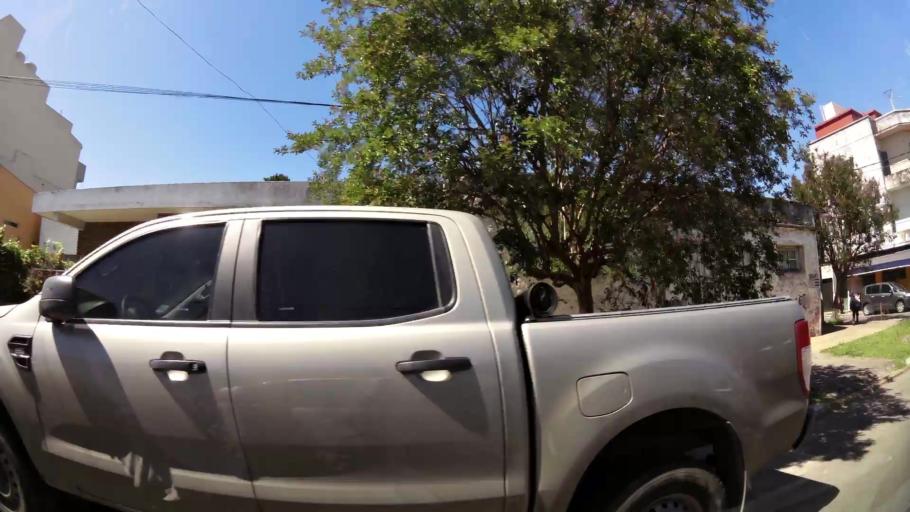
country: AR
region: Buenos Aires
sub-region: Partido de Quilmes
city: Quilmes
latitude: -34.7148
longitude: -58.2707
